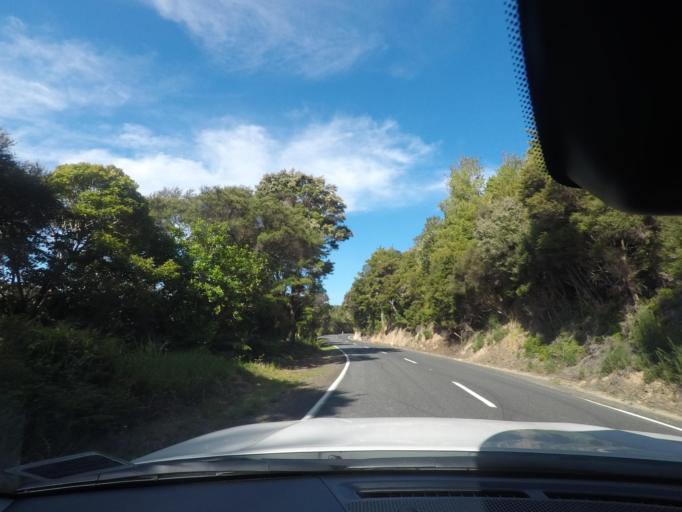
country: NZ
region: Northland
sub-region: Whangarei
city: Ngunguru
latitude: -35.6643
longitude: 174.4799
